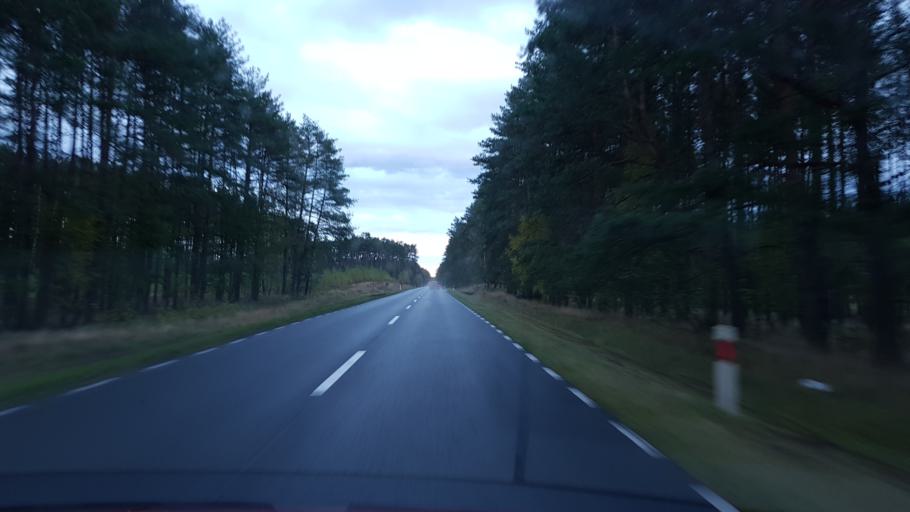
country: PL
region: Greater Poland Voivodeship
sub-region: Powiat pilski
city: Smilowo
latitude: 53.2057
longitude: 16.8452
